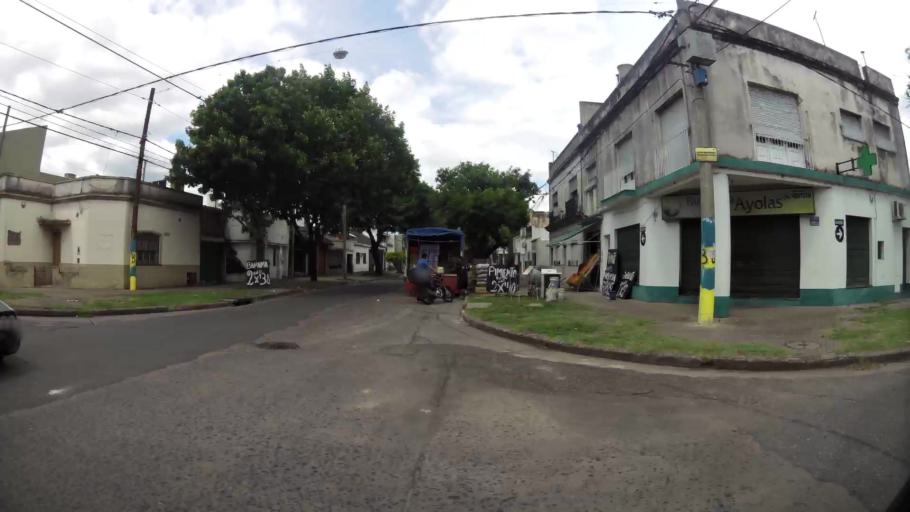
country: AR
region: Santa Fe
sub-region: Departamento de Rosario
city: Rosario
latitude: -32.9754
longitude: -60.6542
